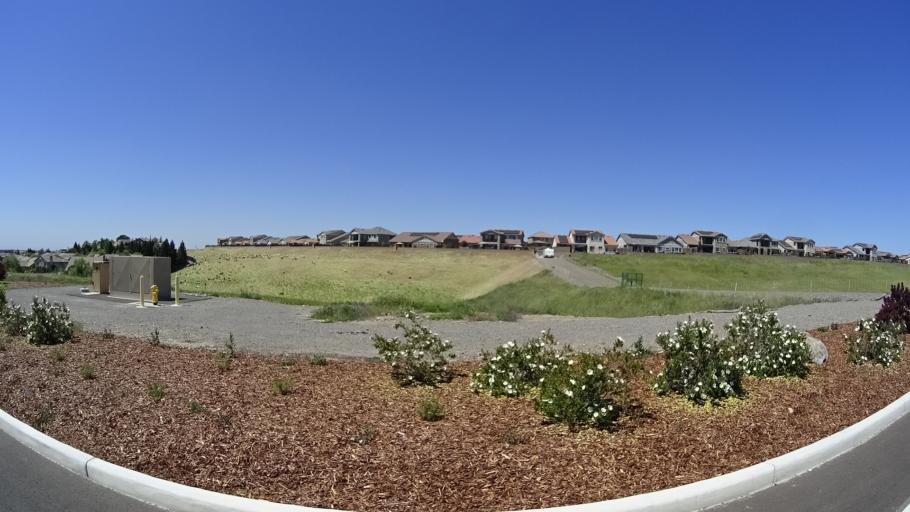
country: US
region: California
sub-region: Placer County
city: Rocklin
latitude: 38.8244
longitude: -121.2691
